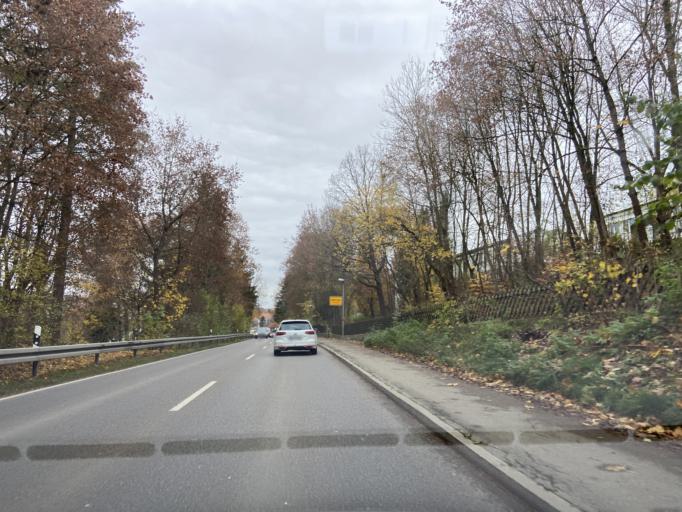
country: DE
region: Baden-Wuerttemberg
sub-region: Tuebingen Region
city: Sigmaringen
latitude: 48.0848
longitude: 9.2294
